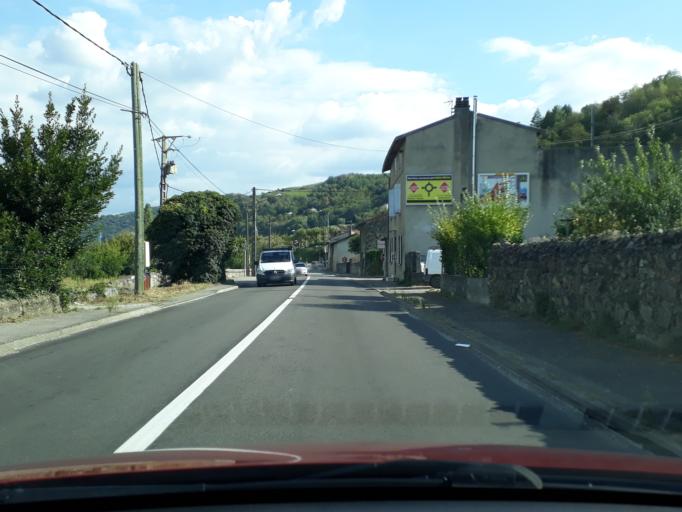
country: FR
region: Rhone-Alpes
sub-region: Departement de l'Ardeche
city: Serrieres
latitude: 45.3240
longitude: 4.7598
